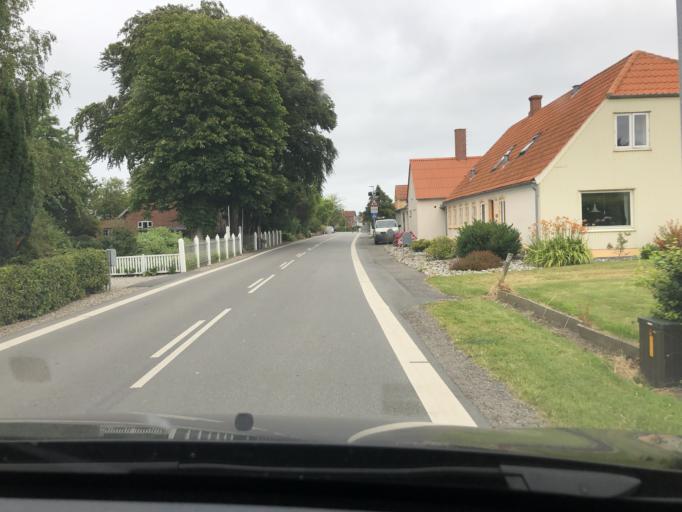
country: DK
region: South Denmark
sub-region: AEro Kommune
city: Marstal
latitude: 54.8555
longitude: 10.5075
